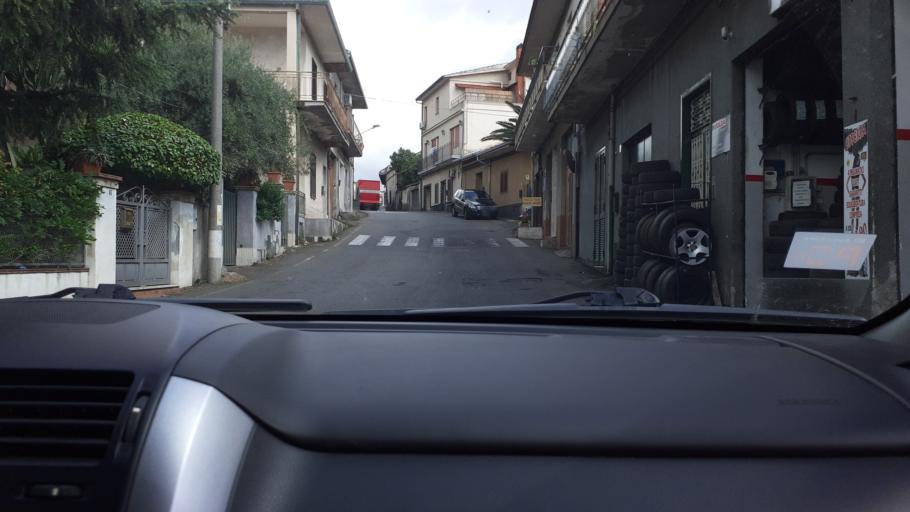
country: IT
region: Sicily
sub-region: Catania
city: San Gregorio di Catania
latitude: 37.5622
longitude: 15.1059
